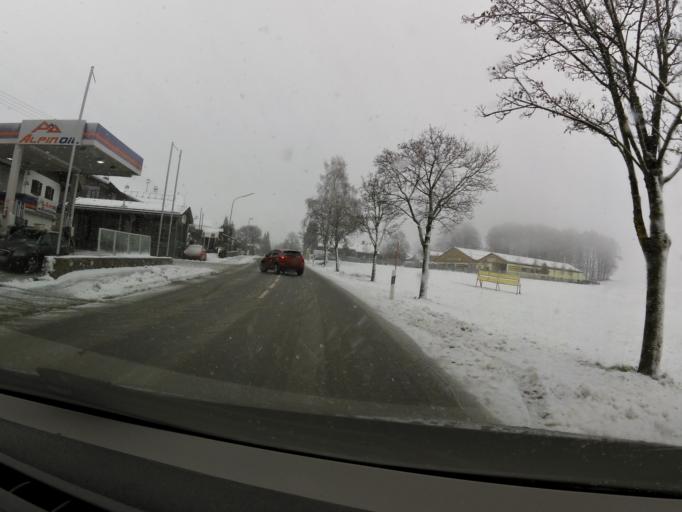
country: DE
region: Bavaria
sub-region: Upper Bavaria
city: Waakirchen
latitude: 47.7690
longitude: 11.6792
